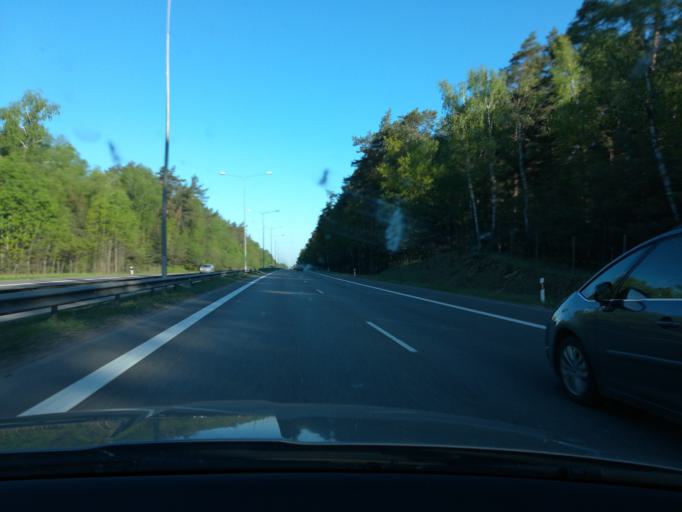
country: LT
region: Kauno apskritis
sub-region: Kauno rajonas
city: Karmelava
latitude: 54.8901
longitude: 24.1667
